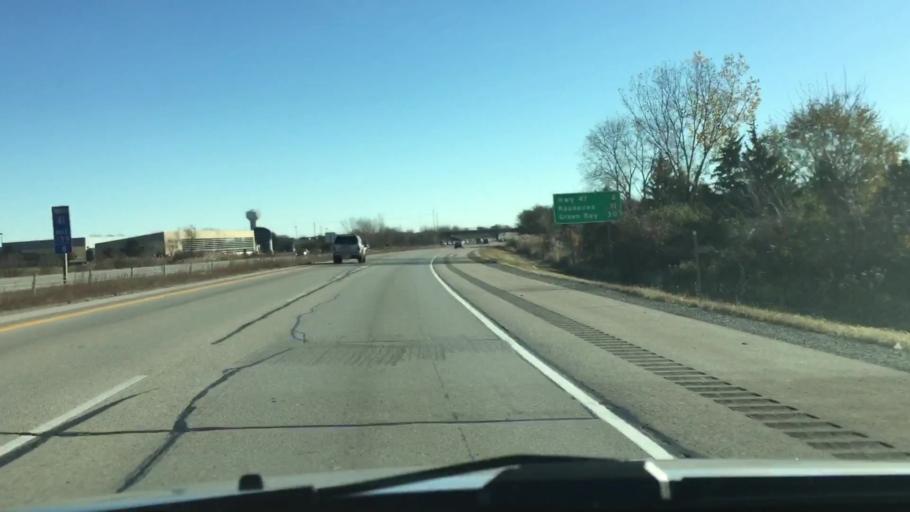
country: US
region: Wisconsin
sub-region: Outagamie County
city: Appleton
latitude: 44.2989
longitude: -88.4536
